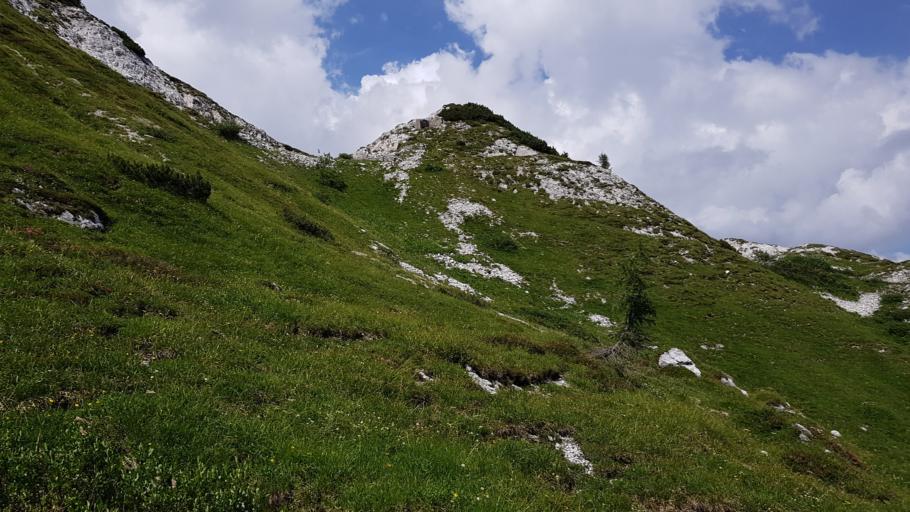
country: SI
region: Bovec
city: Bovec
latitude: 46.3836
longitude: 13.5168
